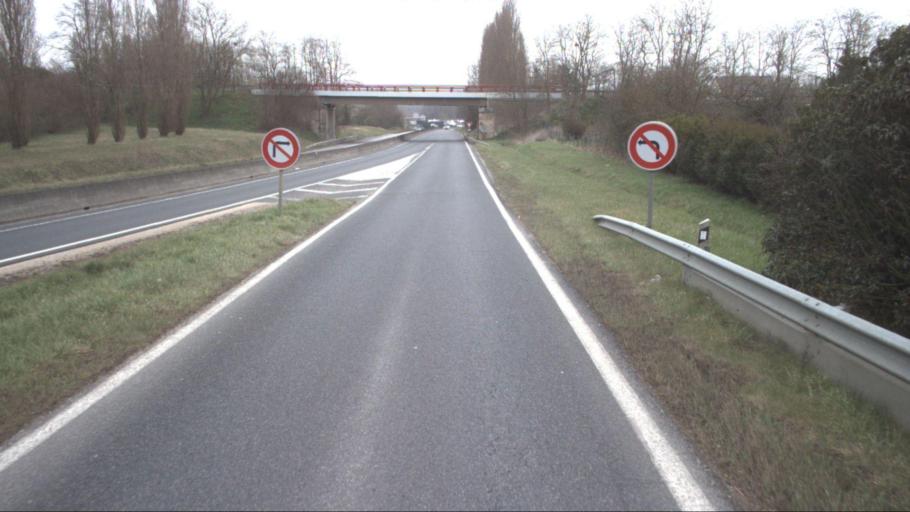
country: FR
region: Ile-de-France
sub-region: Departement des Yvelines
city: Ablis
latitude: 48.5170
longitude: 1.8271
